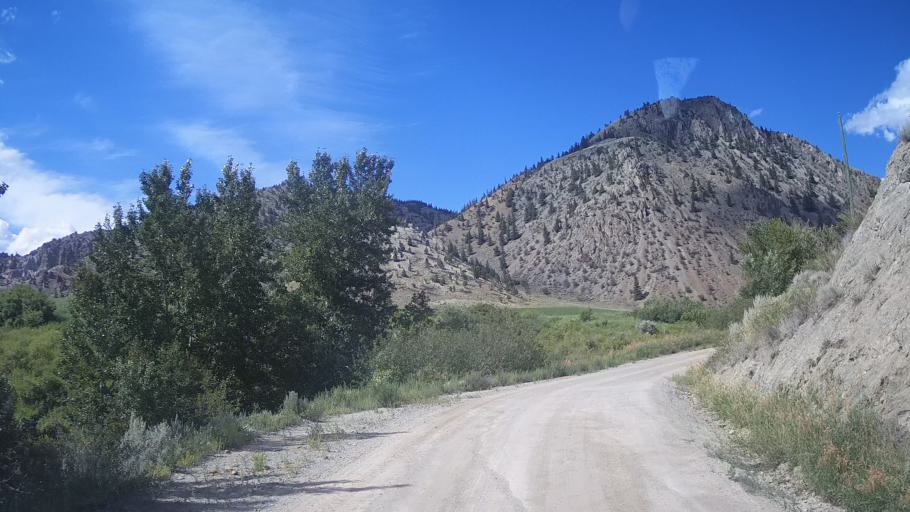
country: CA
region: British Columbia
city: Lillooet
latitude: 51.1926
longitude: -122.1178
